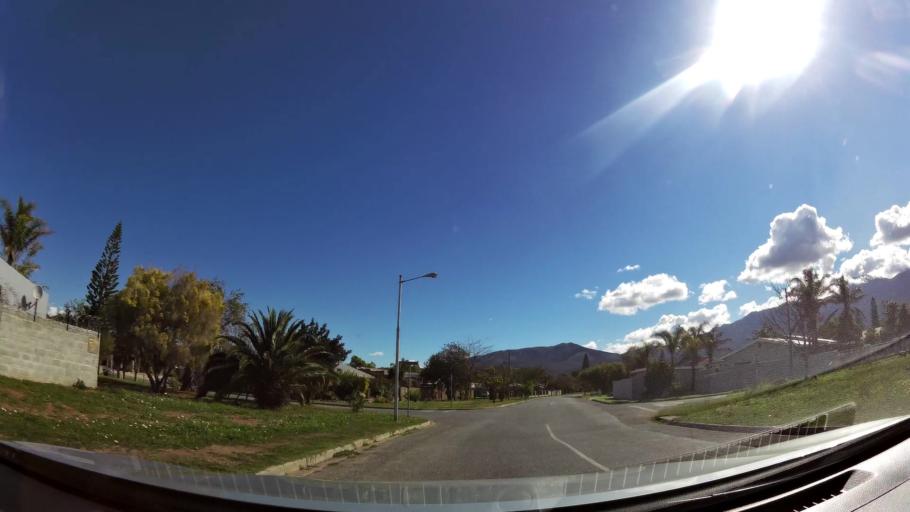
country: ZA
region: Western Cape
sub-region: Cape Winelands District Municipality
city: Ashton
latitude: -33.8098
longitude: 19.8979
